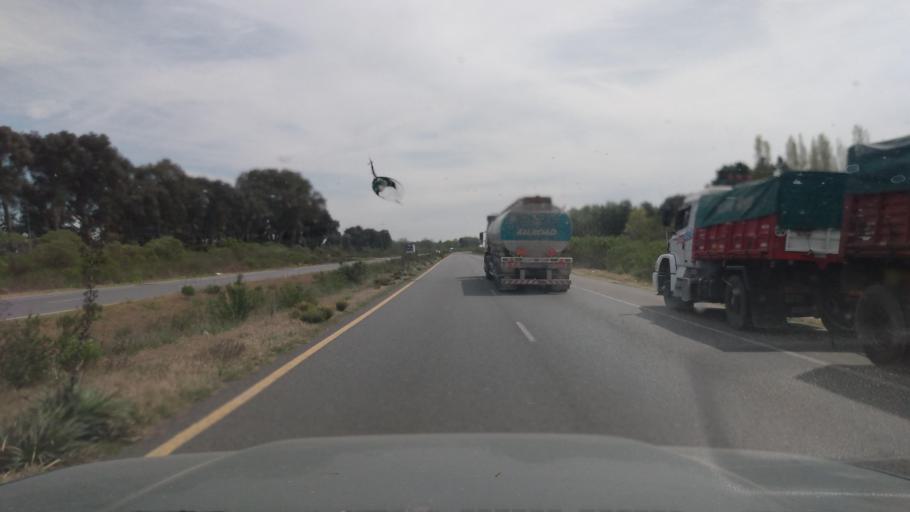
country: AR
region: Buenos Aires
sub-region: Partido de Lujan
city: Lujan
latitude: -34.4995
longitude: -59.0482
